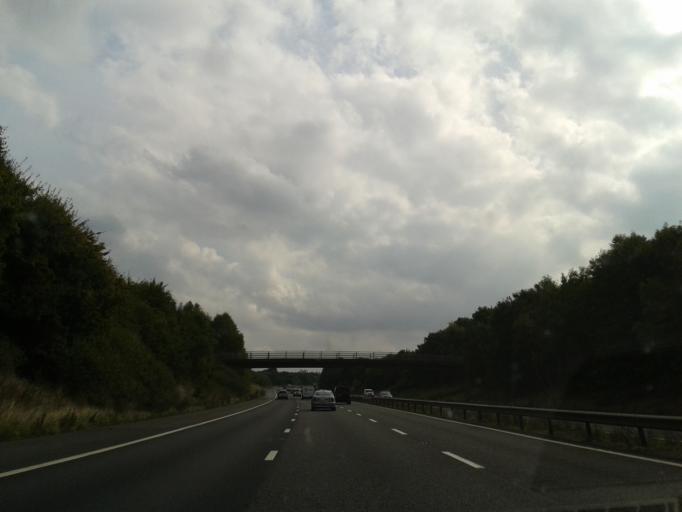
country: GB
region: England
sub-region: Warwickshire
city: Wroxall
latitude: 52.3089
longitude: -1.7070
